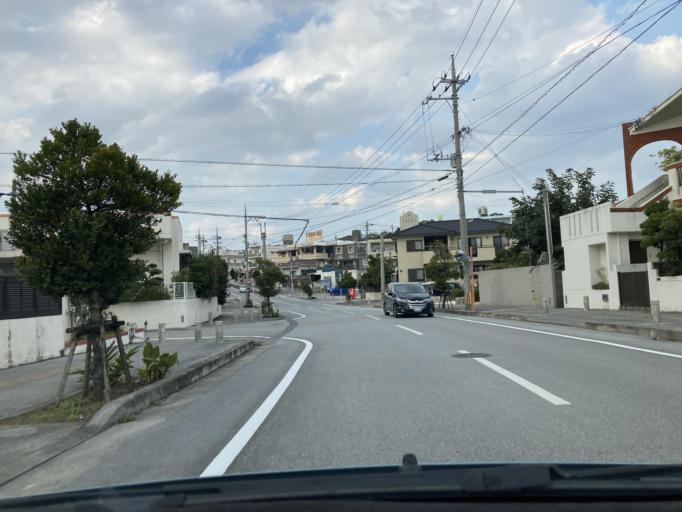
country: JP
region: Okinawa
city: Tomigusuku
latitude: 26.1950
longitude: 127.7335
